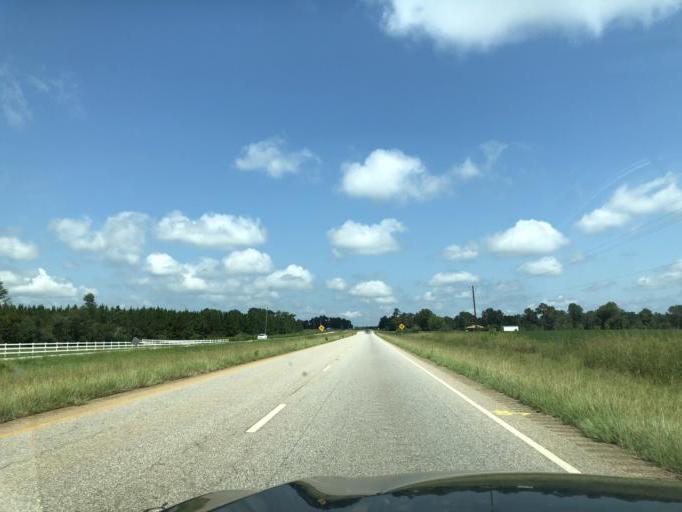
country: US
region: Alabama
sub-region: Henry County
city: Abbeville
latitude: 31.6128
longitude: -85.2772
